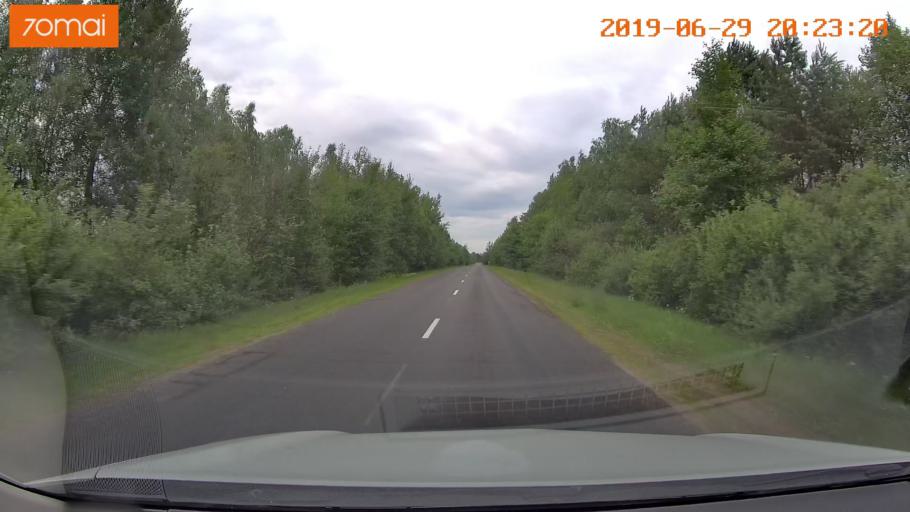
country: BY
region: Brest
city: Asnyezhytsy
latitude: 52.4431
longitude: 26.2599
